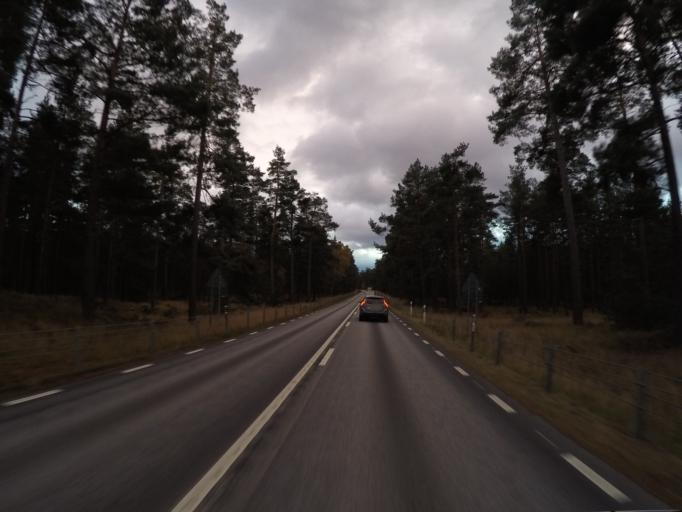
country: SE
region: Skane
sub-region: Kristianstads Kommun
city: Degeberga
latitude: 55.8728
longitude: 14.0893
